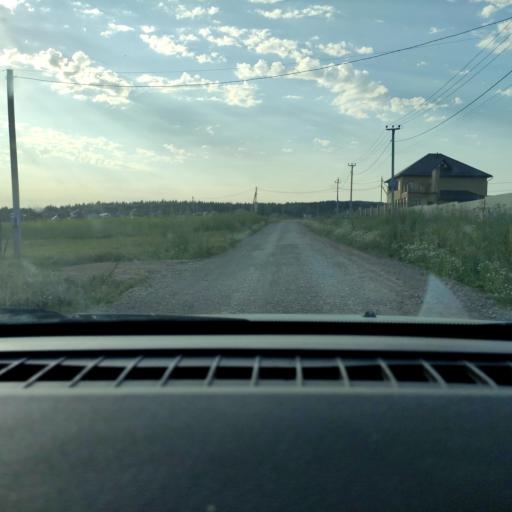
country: RU
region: Perm
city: Ferma
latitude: 57.9502
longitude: 56.3570
